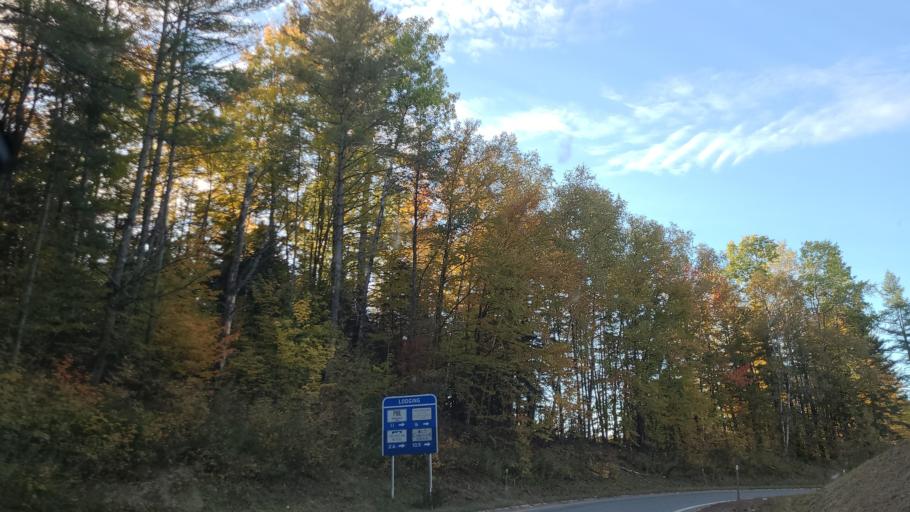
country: US
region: New Hampshire
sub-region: Grafton County
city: Littleton
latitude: 44.2832
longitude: -71.7452
